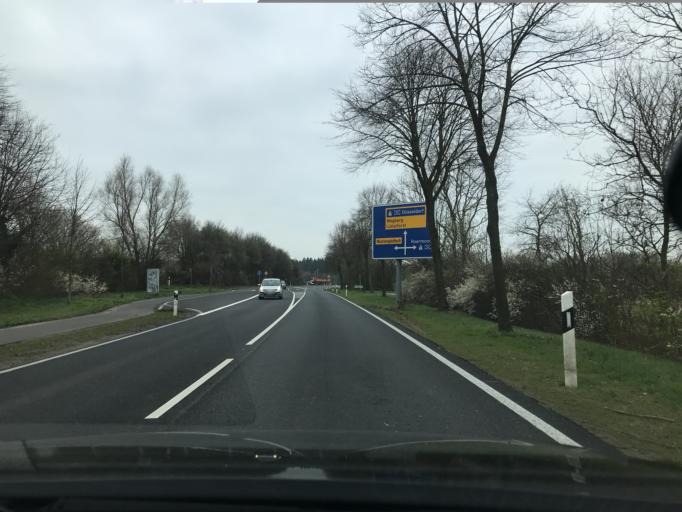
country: DE
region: North Rhine-Westphalia
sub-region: Regierungsbezirk Dusseldorf
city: Schwalmtal
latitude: 51.2087
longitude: 6.2606
